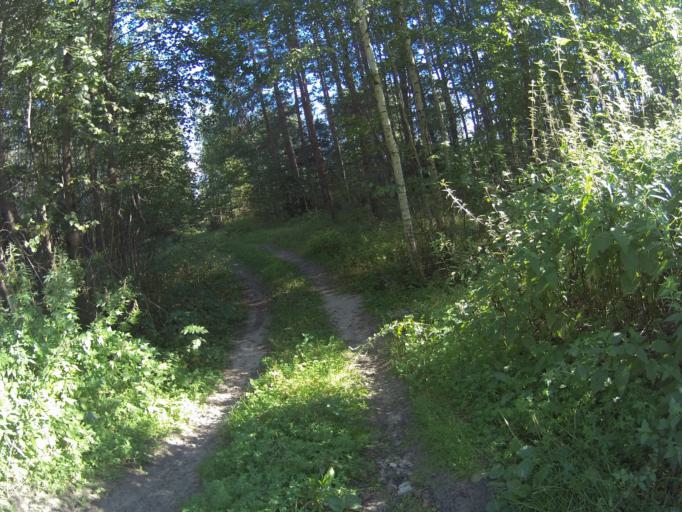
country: RU
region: Vladimir
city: Gusevskiy
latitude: 55.5760
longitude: 40.5153
